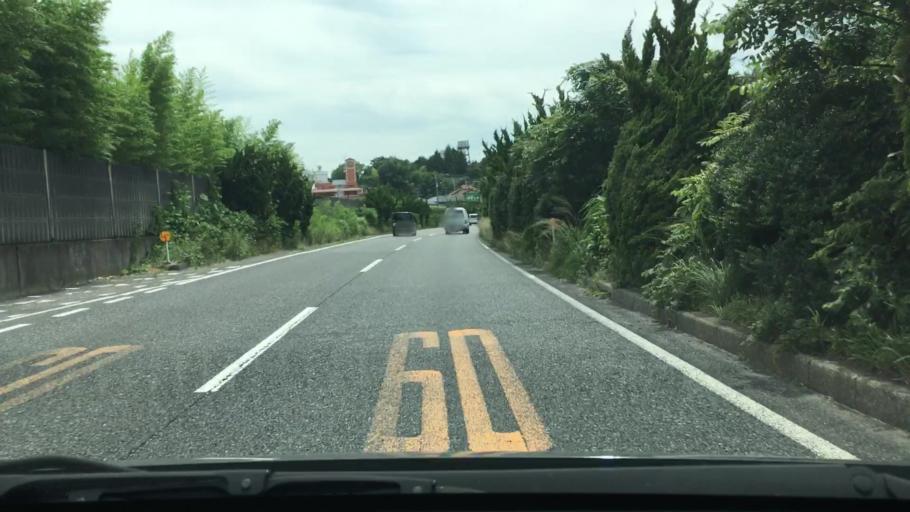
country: JP
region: Hiroshima
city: Hatsukaichi
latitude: 34.3755
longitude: 132.3443
